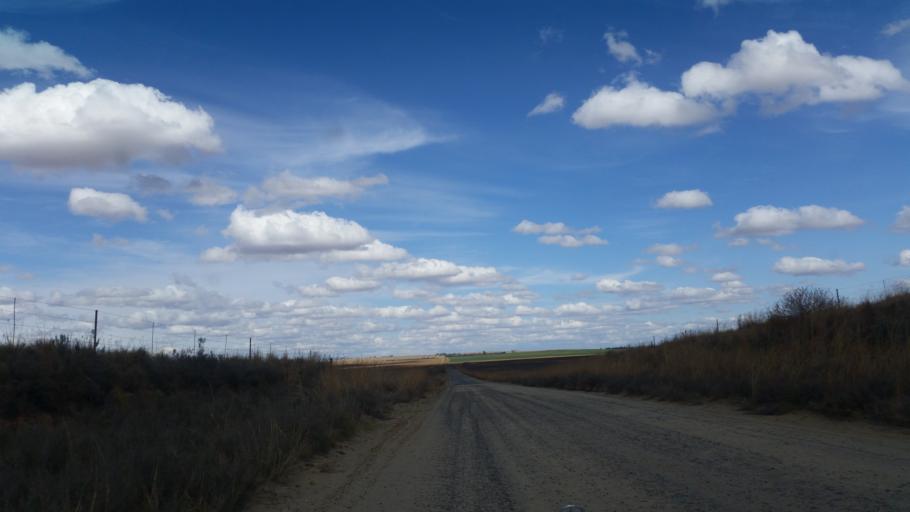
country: ZA
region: Orange Free State
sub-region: Thabo Mofutsanyana District Municipality
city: Bethlehem
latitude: -28.1584
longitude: 28.6731
